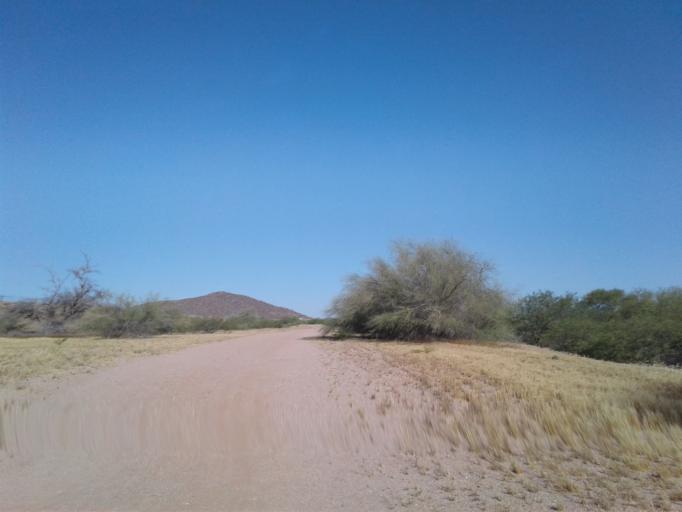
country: US
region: Arizona
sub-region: Maricopa County
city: Paradise Valley
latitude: 33.6780
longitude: -112.0174
